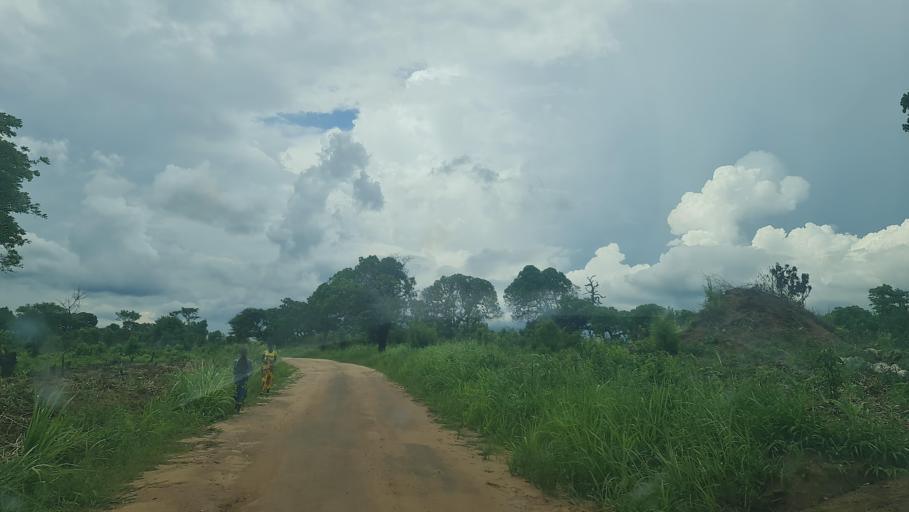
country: MW
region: Southern Region
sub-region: Nsanje District
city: Nsanje
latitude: -17.5826
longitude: 35.6648
